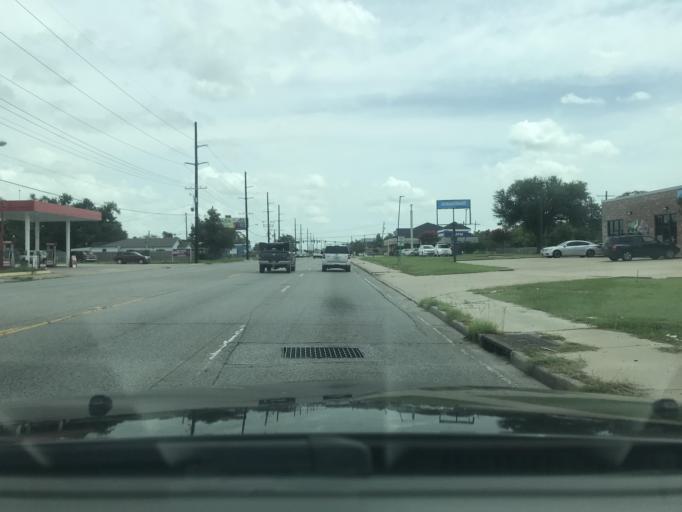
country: US
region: Louisiana
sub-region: Calcasieu Parish
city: Lake Charles
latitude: 30.2151
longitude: -93.1802
